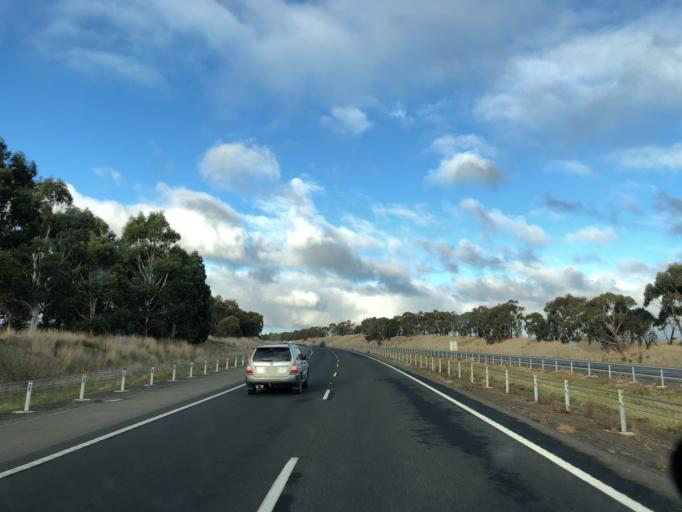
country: AU
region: Victoria
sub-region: Mount Alexander
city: Castlemaine
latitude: -37.2241
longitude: 144.4228
